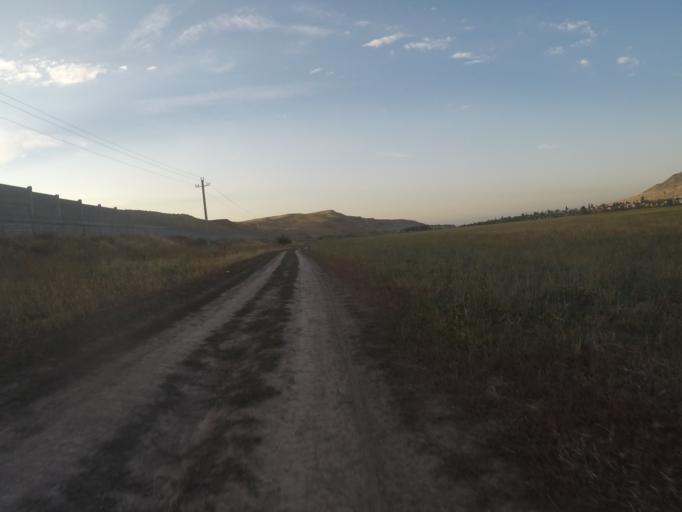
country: KG
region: Chuy
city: Bishkek
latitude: 42.7543
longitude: 74.6366
